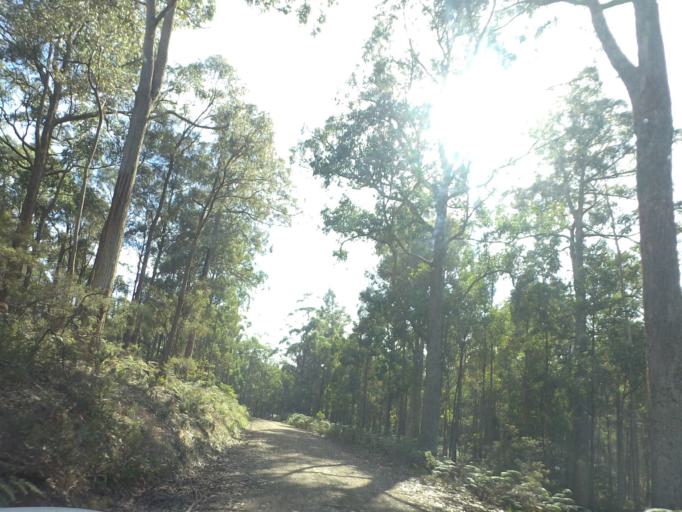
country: AU
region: Victoria
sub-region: Moorabool
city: Bacchus Marsh
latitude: -37.4293
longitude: 144.2406
